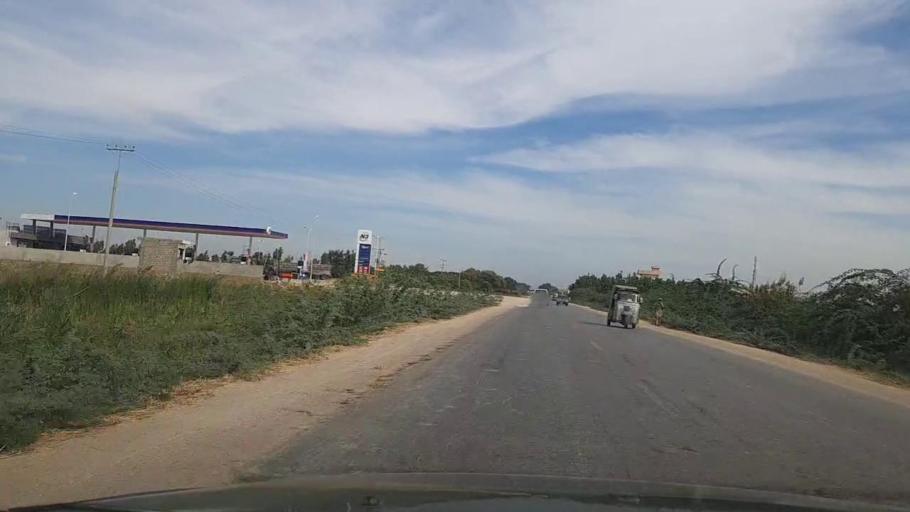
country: PK
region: Sindh
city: Thatta
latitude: 24.7874
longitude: 67.9535
